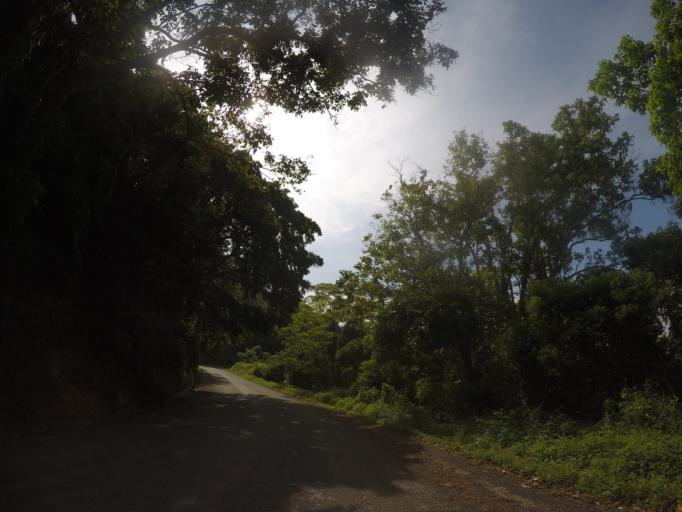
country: MX
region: Oaxaca
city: Pluma Hidalgo
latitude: 15.9381
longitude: -96.4381
